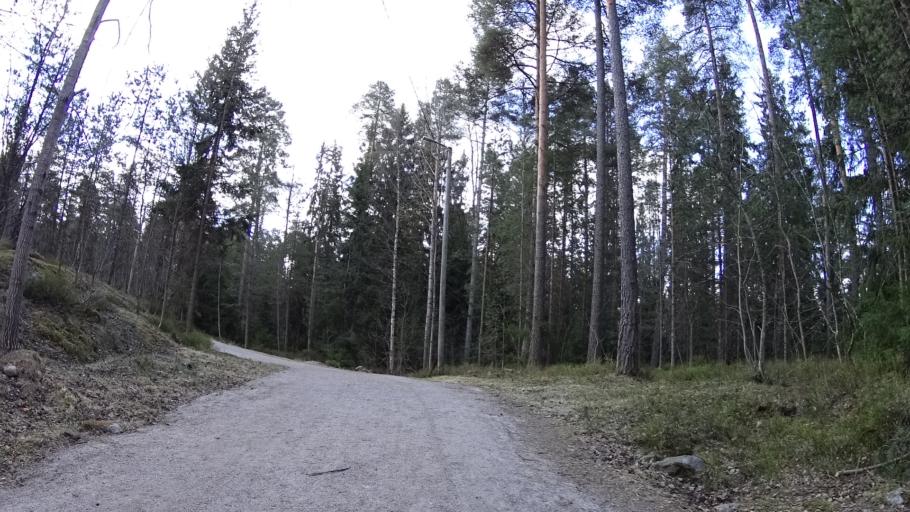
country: FI
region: Uusimaa
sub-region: Helsinki
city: Kilo
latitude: 60.2304
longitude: 24.7987
